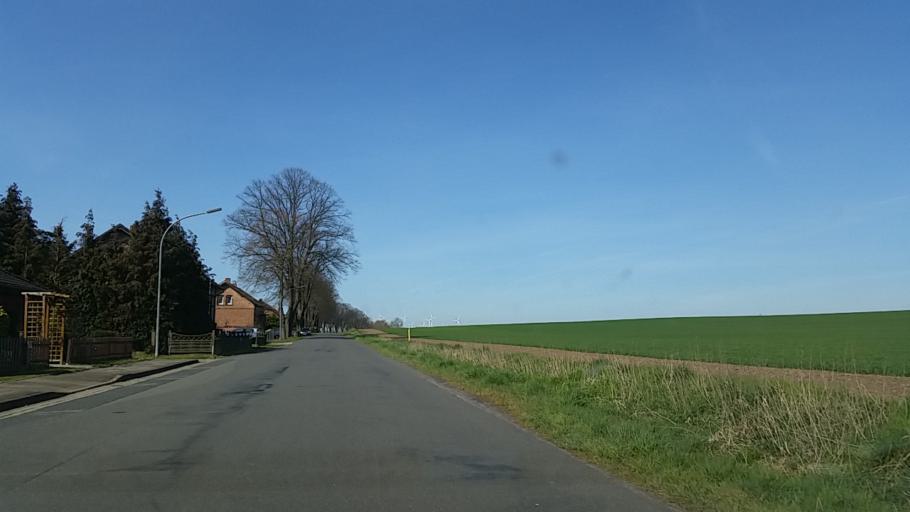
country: DE
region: Lower Saxony
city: Beierstedt
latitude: 52.0673
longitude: 10.8745
